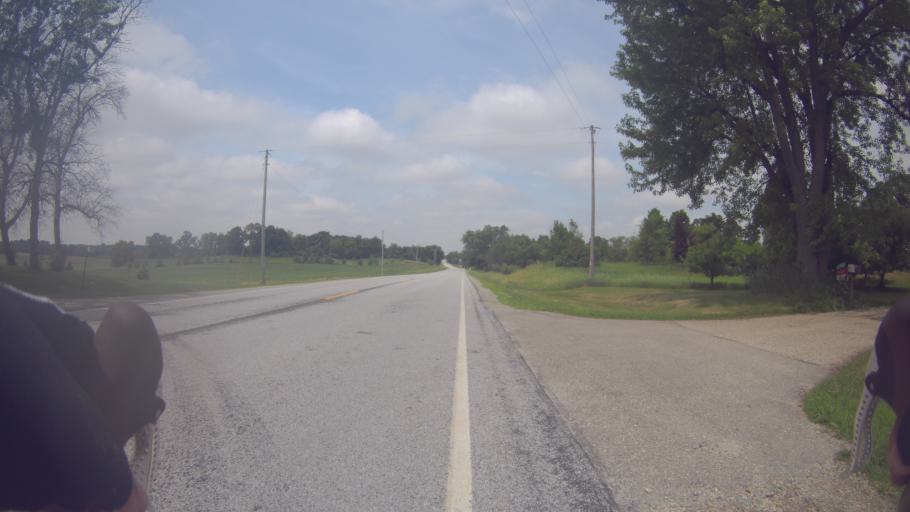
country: US
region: Wisconsin
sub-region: Jefferson County
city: Lake Ripley
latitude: 42.9498
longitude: -88.9909
